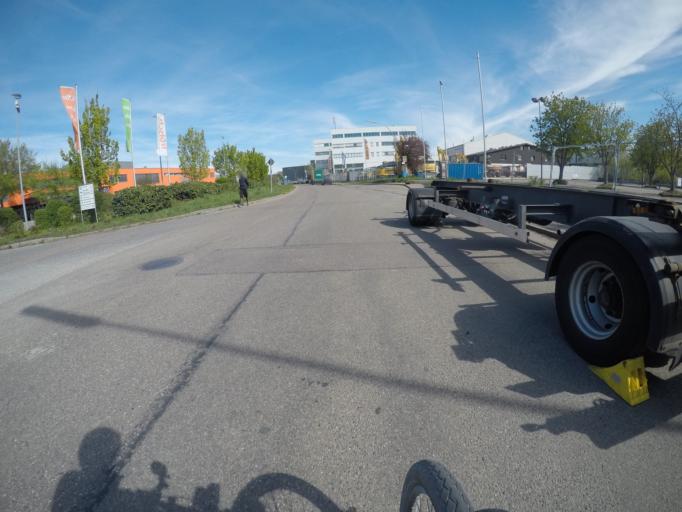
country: DE
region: Baden-Wuerttemberg
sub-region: Regierungsbezirk Stuttgart
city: Korntal
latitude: 48.8525
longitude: 9.1106
